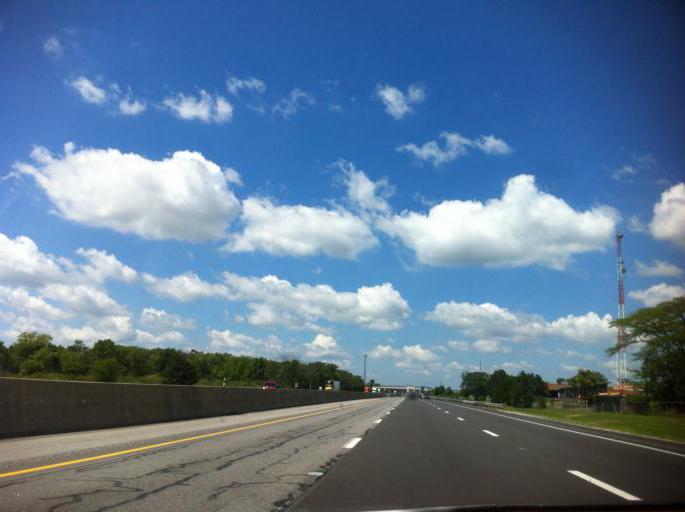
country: US
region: Ohio
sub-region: Ottawa County
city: Elmore
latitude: 41.4699
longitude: -83.3178
